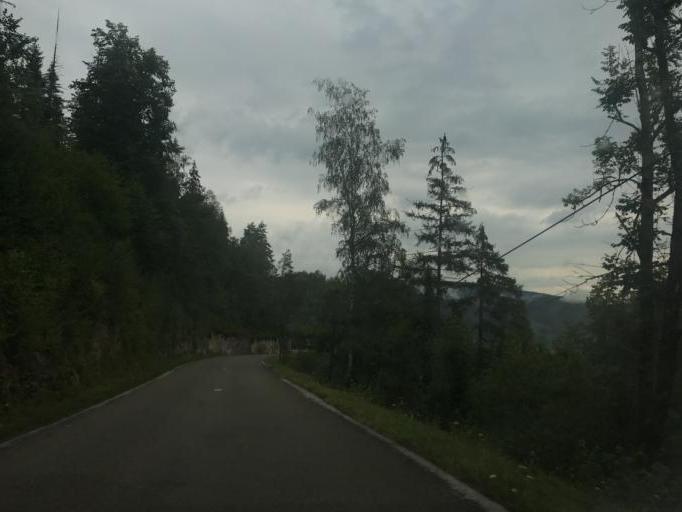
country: FR
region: Franche-Comte
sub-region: Departement du Jura
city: Lavans-les-Saint-Claude
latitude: 46.3468
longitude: 5.7673
